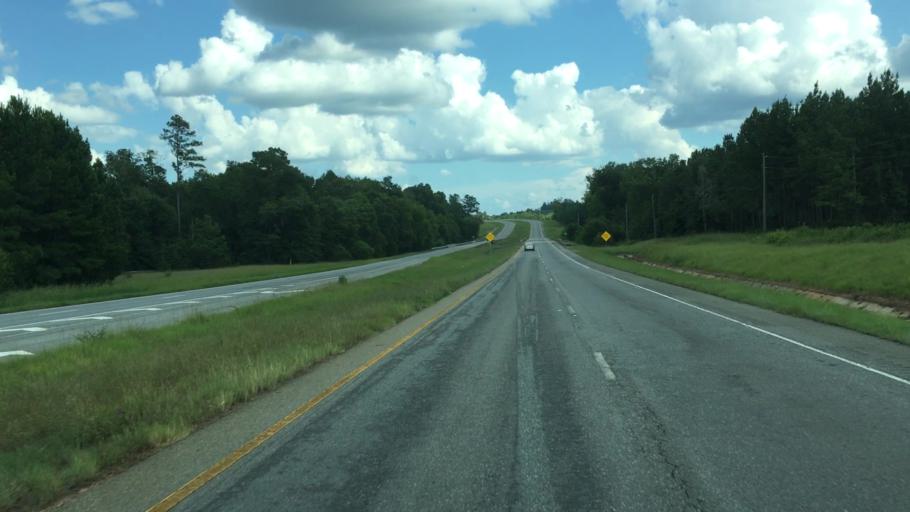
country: US
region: Georgia
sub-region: Wilkinson County
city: Irwinton
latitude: 32.7015
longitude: -83.1237
